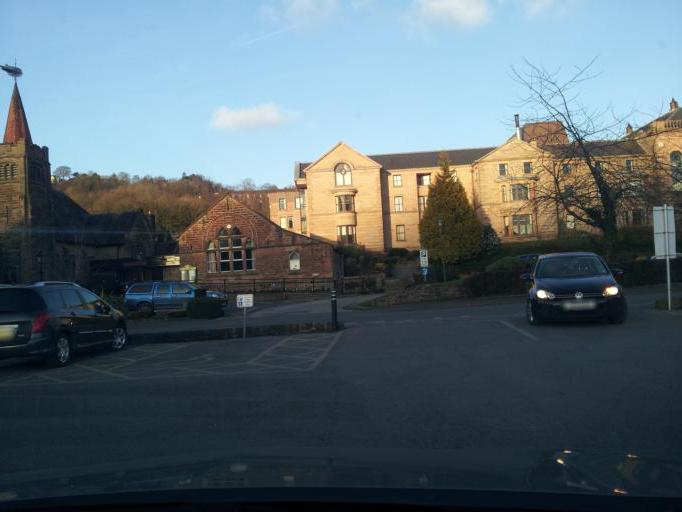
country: GB
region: England
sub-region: Derbyshire
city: Matlock
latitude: 53.1391
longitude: -1.5554
